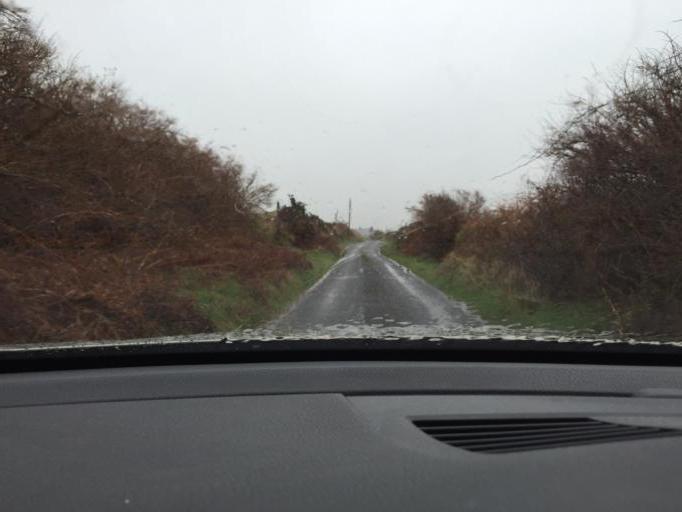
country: IE
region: Munster
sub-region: Ciarrai
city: Dingle
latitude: 52.1379
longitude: -10.4077
